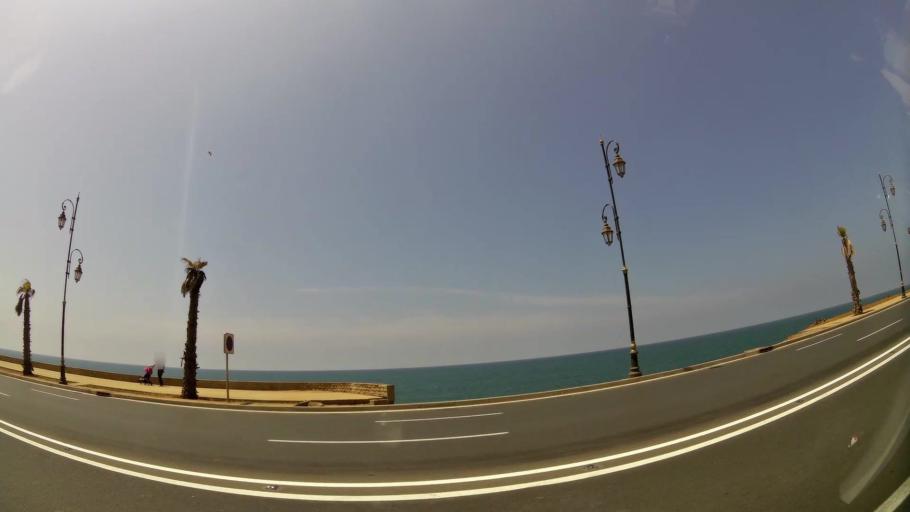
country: MA
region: Rabat-Sale-Zemmour-Zaer
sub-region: Rabat
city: Rabat
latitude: 34.0106
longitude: -6.8658
